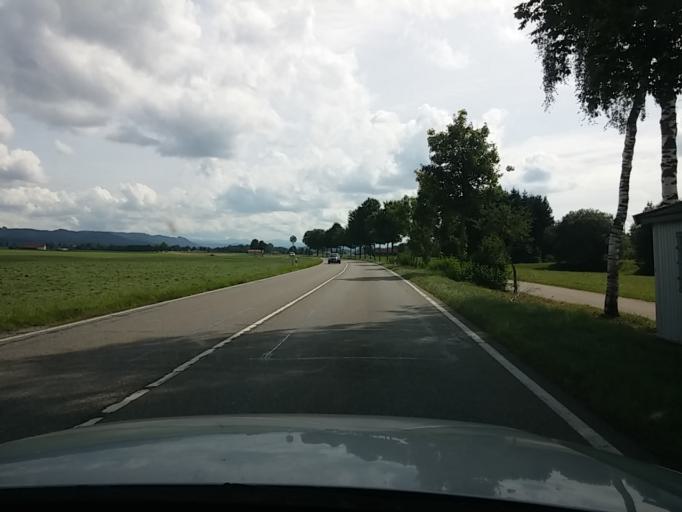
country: DE
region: Baden-Wuerttemberg
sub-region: Tuebingen Region
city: Leutkirch im Allgau
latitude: 47.7857
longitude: 10.0441
